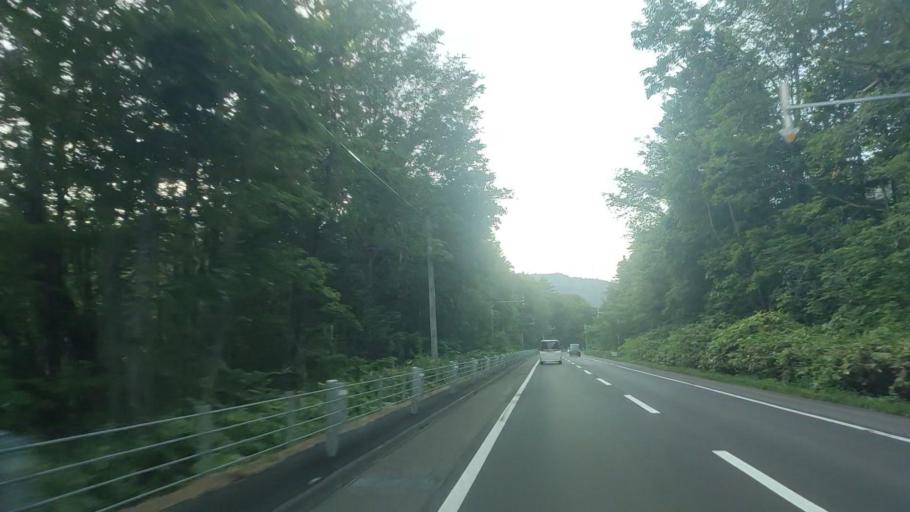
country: JP
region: Hokkaido
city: Ashibetsu
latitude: 43.3360
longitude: 142.1524
